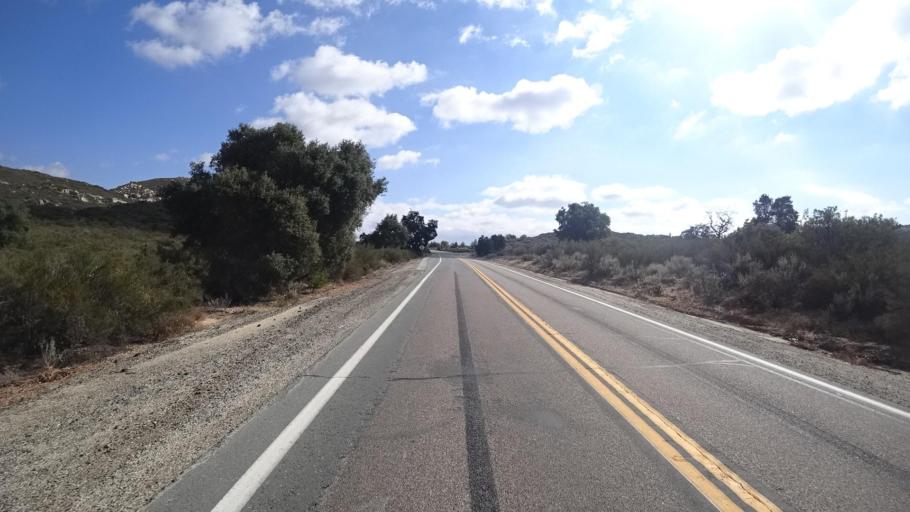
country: US
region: California
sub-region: San Diego County
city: Campo
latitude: 32.6926
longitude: -116.4895
